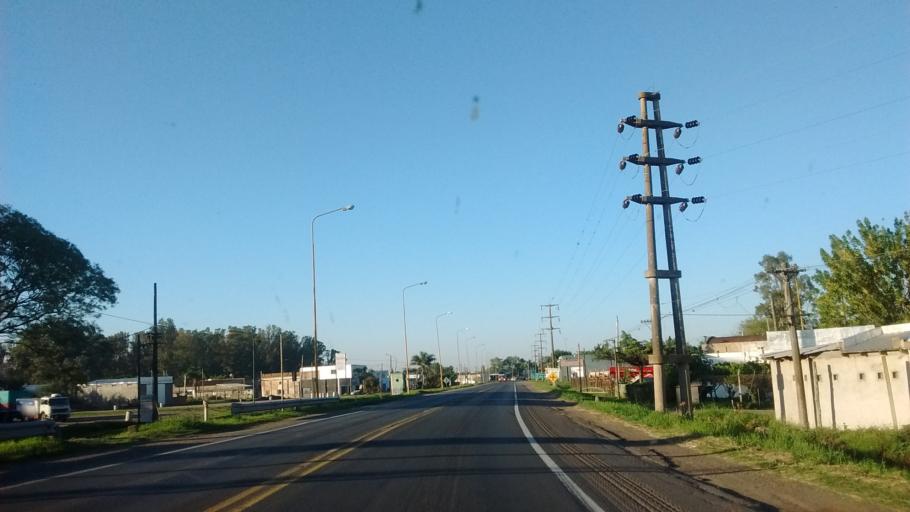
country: AR
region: Santa Fe
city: Firmat
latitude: -33.4446
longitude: -61.4844
